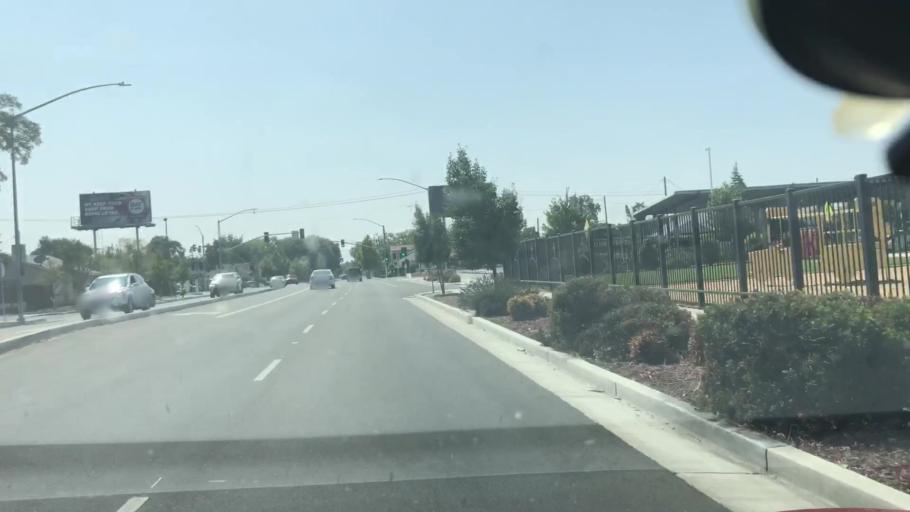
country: US
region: California
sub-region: San Joaquin County
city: Stockton
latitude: 37.9811
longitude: -121.2999
